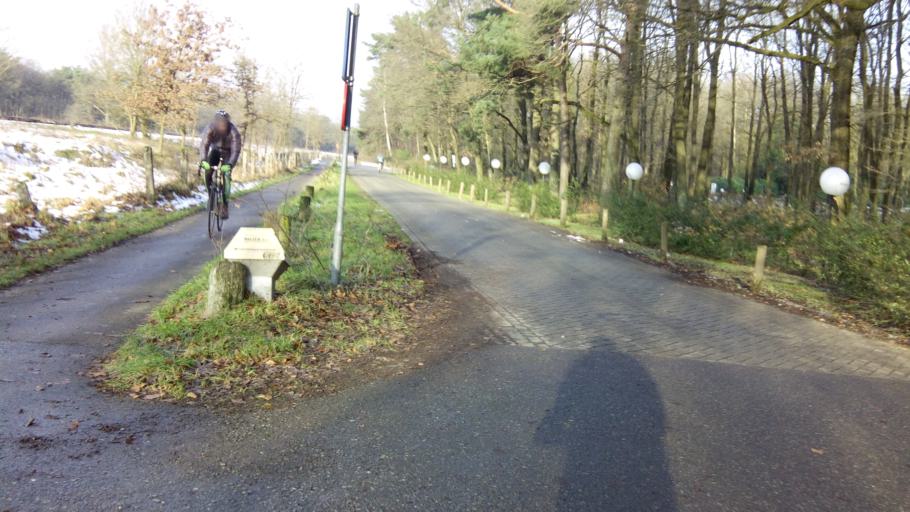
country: NL
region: Gelderland
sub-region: Gemeente Groesbeek
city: Berg en Dal
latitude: 51.7829
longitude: 5.8880
